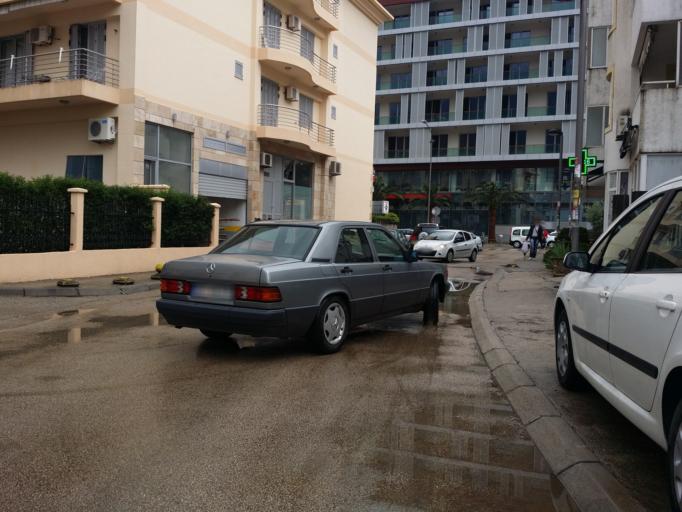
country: ME
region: Budva
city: Budva
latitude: 42.2851
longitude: 18.8382
